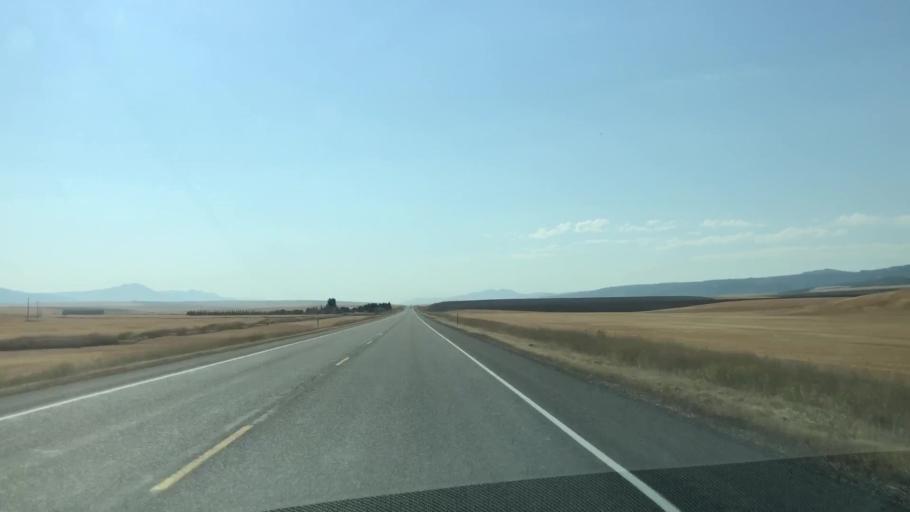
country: US
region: Idaho
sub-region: Madison County
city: Rexburg
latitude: 43.5752
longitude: -111.5626
